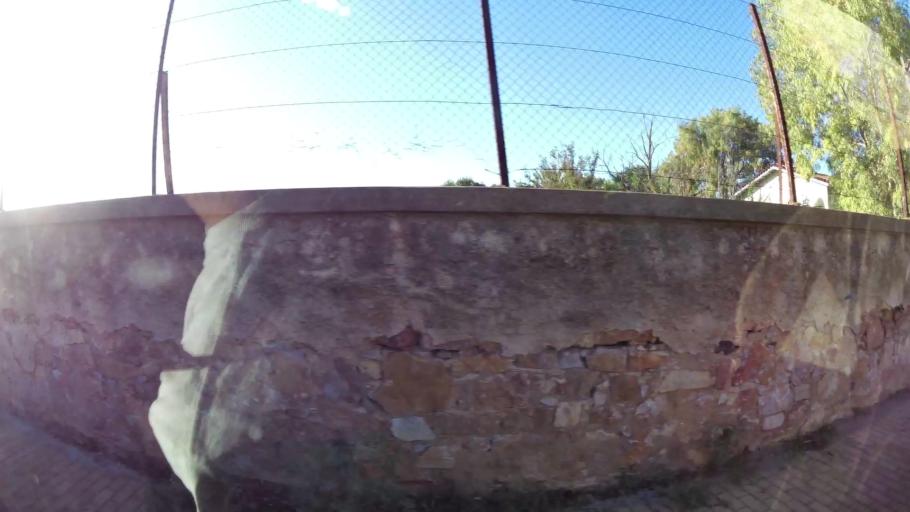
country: GR
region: Attica
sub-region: Nomarchia Anatolikis Attikis
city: Vari
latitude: 37.8248
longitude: 23.8098
